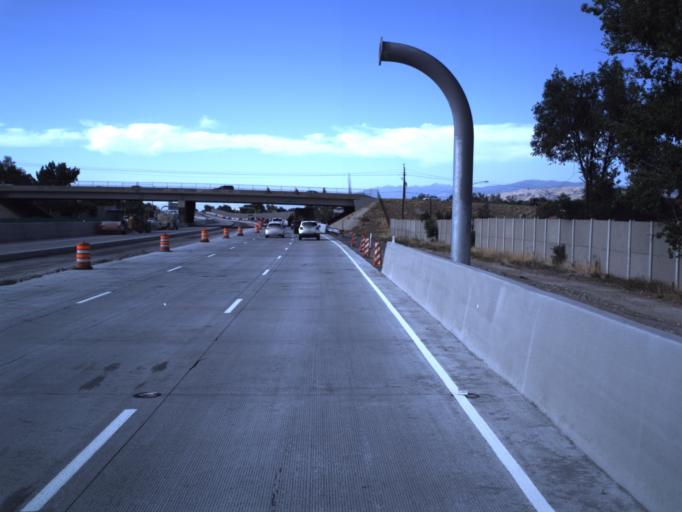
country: US
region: Utah
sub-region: Salt Lake County
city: Taylorsville
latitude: 40.6802
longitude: -111.9514
